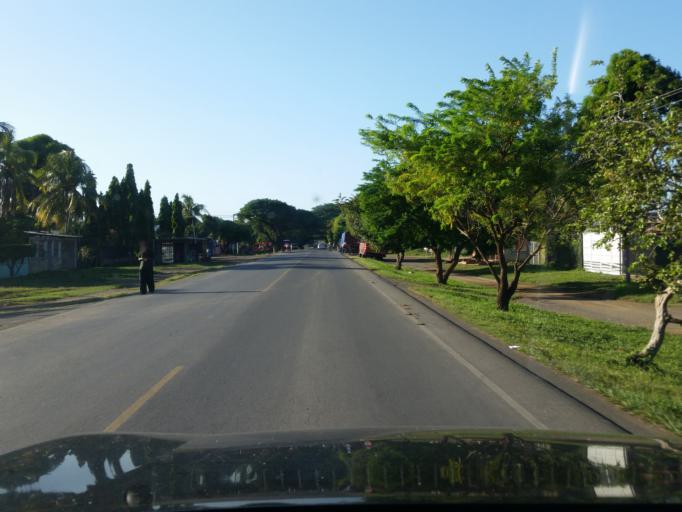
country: NI
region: Rivas
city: Rivas
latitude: 11.4354
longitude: -85.8166
